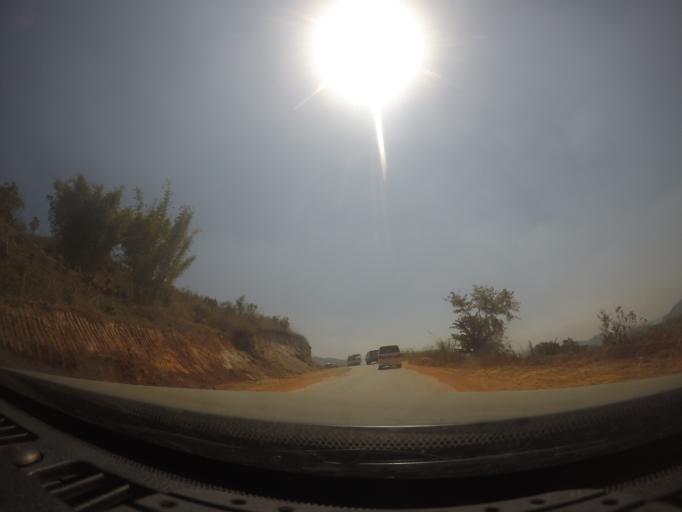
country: MM
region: Shan
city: Taunggyi
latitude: 20.8102
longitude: 97.2750
